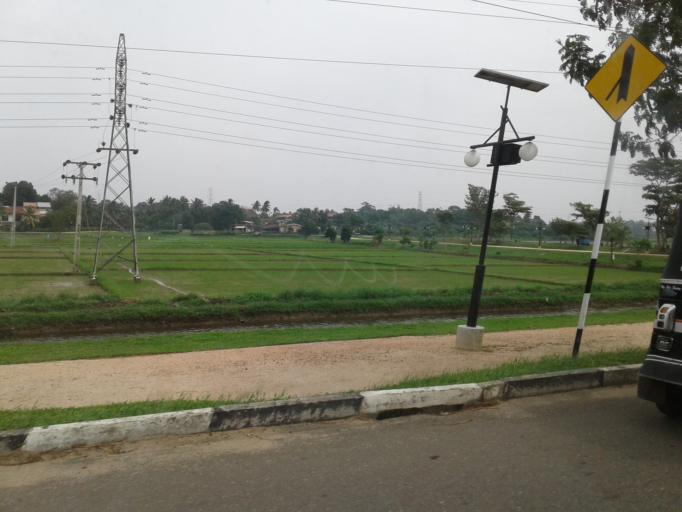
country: LK
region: Western
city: Maharagama
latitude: 6.8673
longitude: 79.9310
